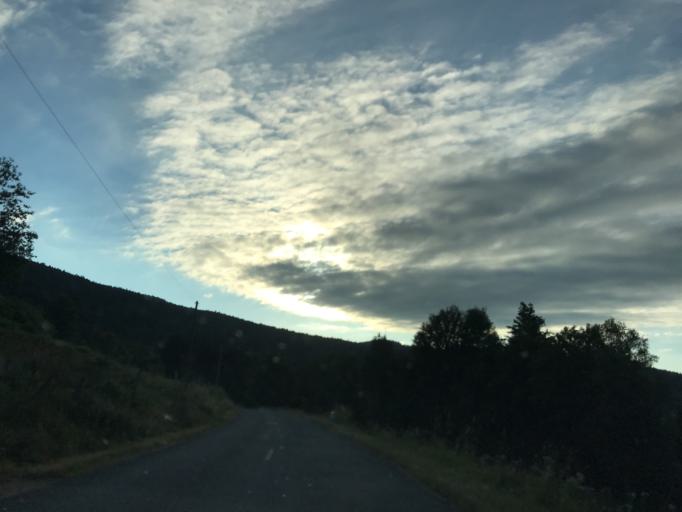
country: FR
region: Rhone-Alpes
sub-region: Departement de la Loire
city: Noiretable
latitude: 45.7464
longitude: 3.8495
